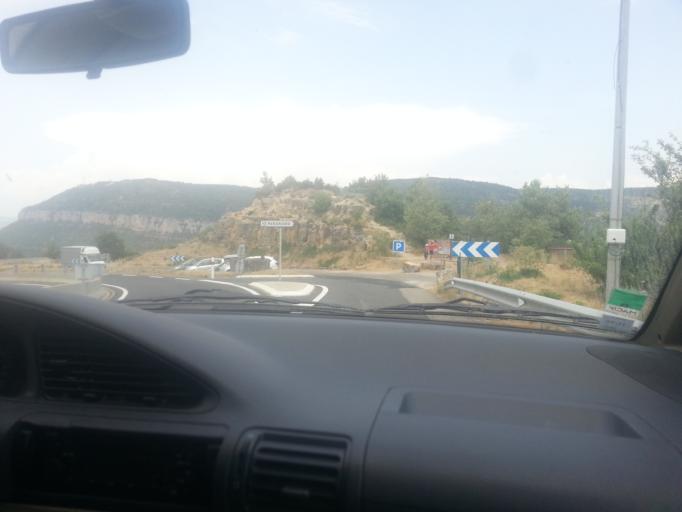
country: FR
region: Midi-Pyrenees
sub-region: Departement de l'Aveyron
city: Millau
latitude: 44.0957
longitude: 3.1241
